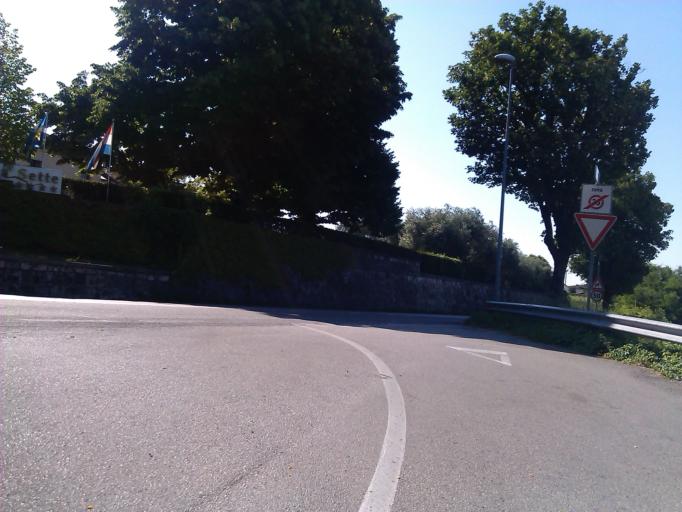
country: IT
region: Veneto
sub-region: Provincia di Vicenza
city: Bassano del Grappa
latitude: 45.7792
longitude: 11.7413
